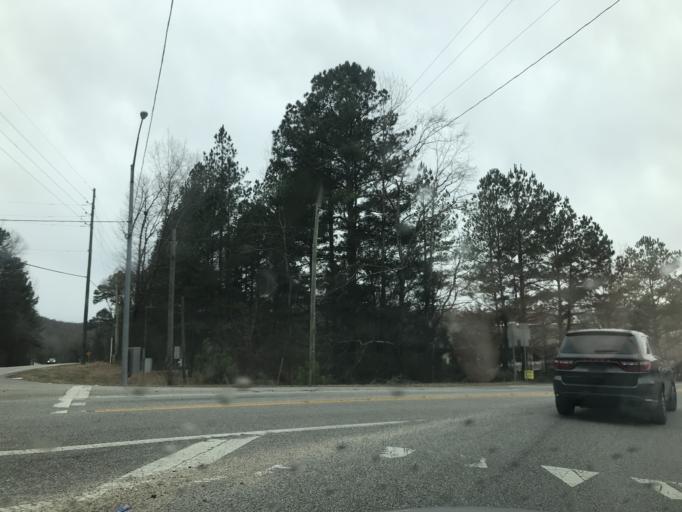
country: US
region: Alabama
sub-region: Shelby County
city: Meadowbrook
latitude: 33.3757
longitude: -86.7049
